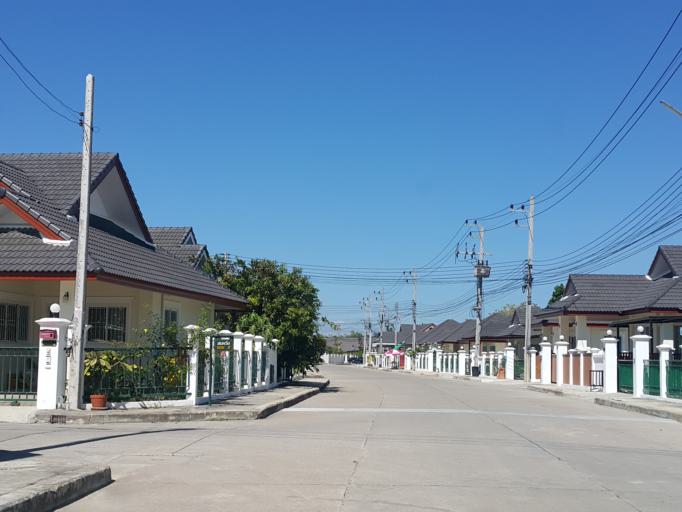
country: TH
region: Chiang Mai
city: San Sai
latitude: 18.7943
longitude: 99.0658
